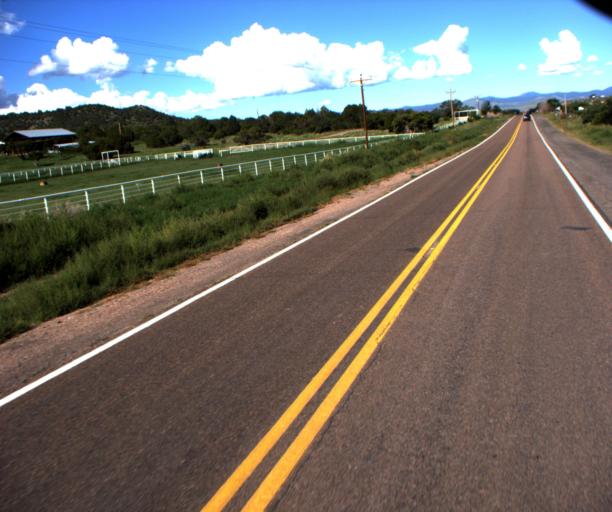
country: US
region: Arizona
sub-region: Apache County
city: Eagar
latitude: 34.1110
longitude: -109.2611
